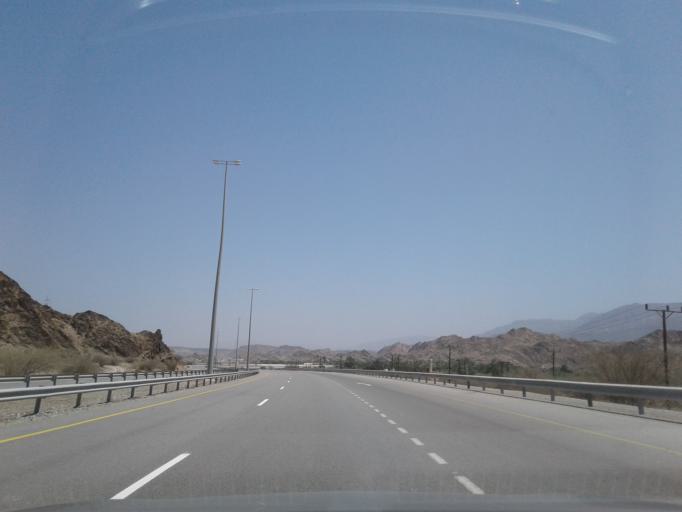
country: OM
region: Muhafazat Masqat
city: Muscat
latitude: 23.2790
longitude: 58.7516
